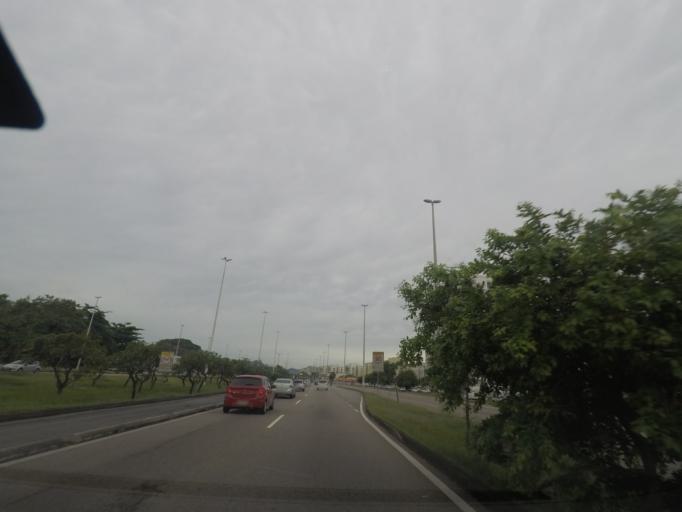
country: BR
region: Rio de Janeiro
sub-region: Nilopolis
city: Nilopolis
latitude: -23.0003
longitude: -43.4153
